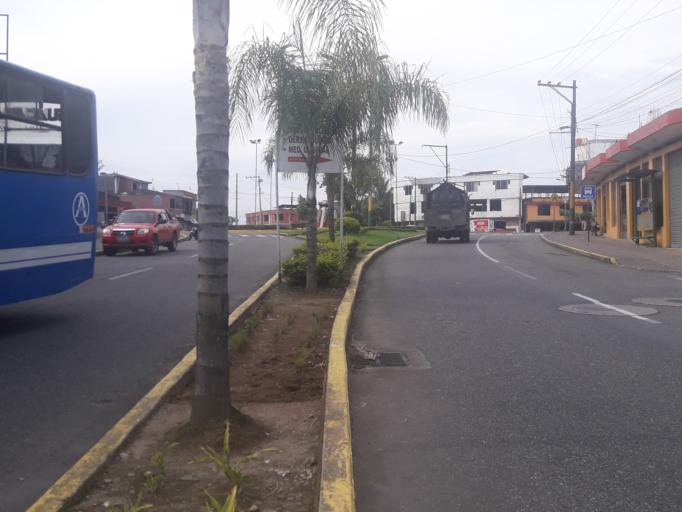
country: EC
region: Napo
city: Tena
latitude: -0.9842
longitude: -77.8127
